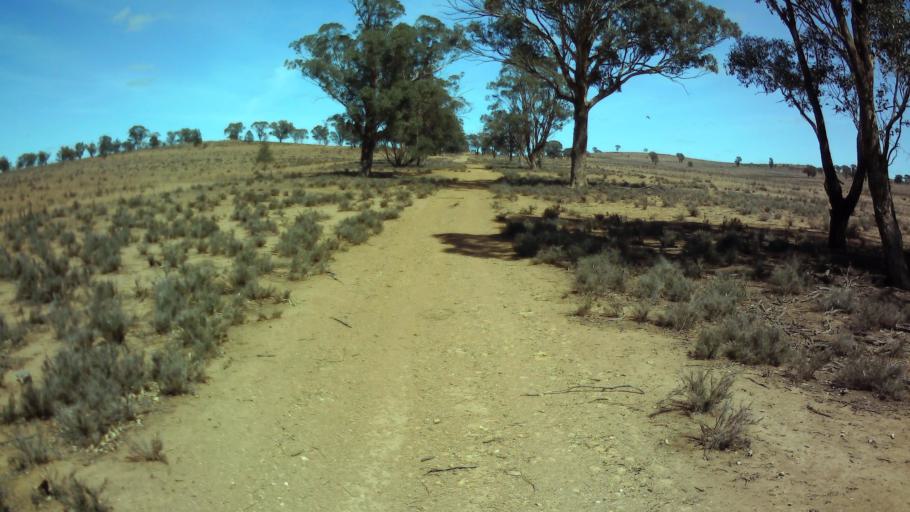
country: AU
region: New South Wales
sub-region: Weddin
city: Grenfell
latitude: -33.7210
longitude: 147.8417
